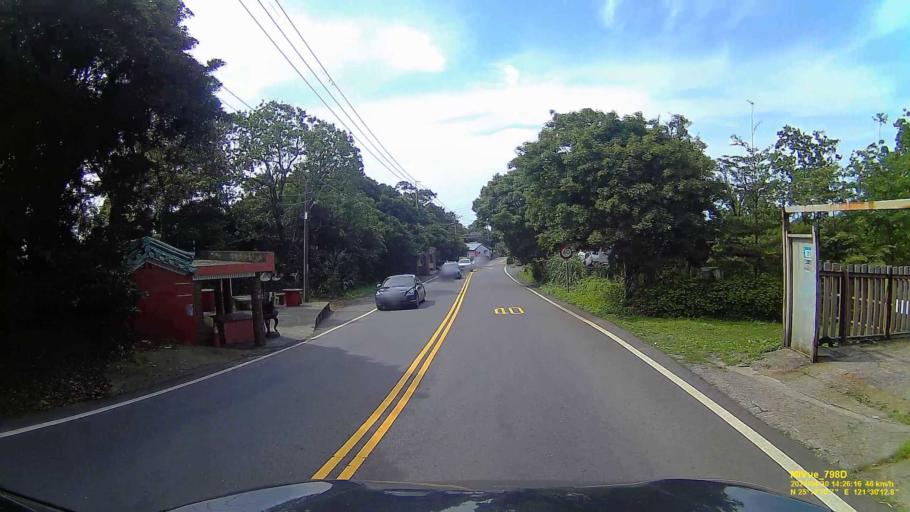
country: TW
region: Taipei
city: Taipei
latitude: 25.2394
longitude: 121.5034
